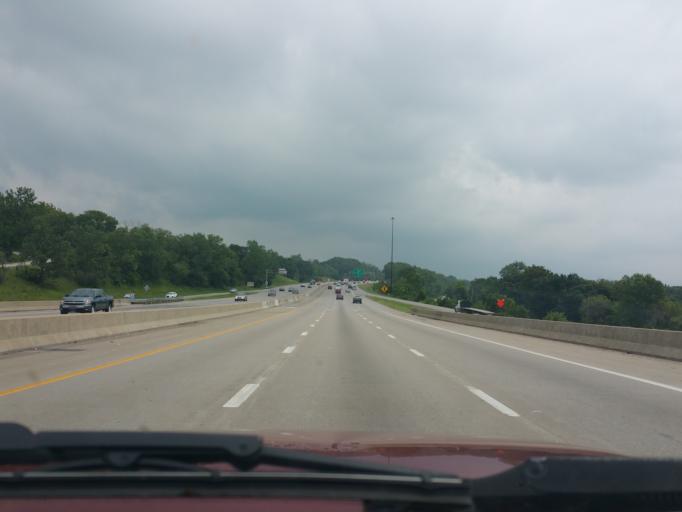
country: US
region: Kansas
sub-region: Johnson County
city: Shawnee
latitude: 39.1053
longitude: -94.7089
